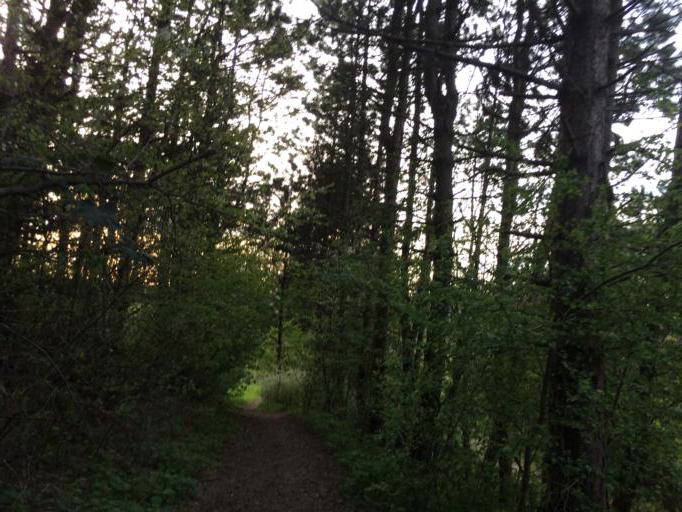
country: DK
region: Capital Region
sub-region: Albertslund Kommune
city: Albertslund
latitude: 55.6468
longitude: 12.3415
